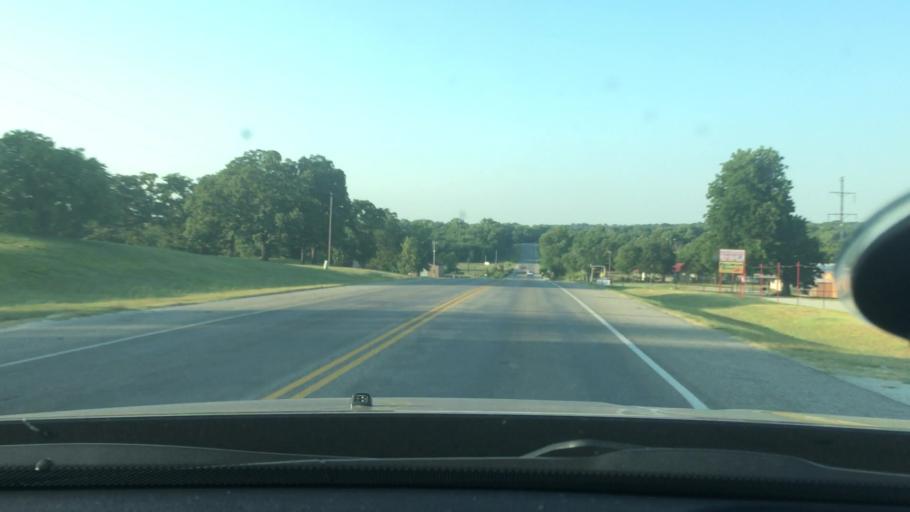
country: US
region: Oklahoma
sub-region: Pontotoc County
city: Byng
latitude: 34.8452
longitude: -96.6786
